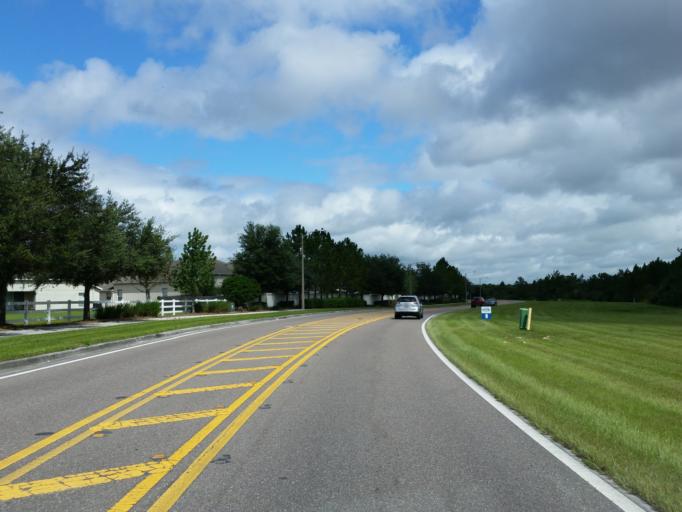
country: US
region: Florida
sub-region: Pasco County
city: Wesley Chapel
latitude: 28.2059
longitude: -82.3005
